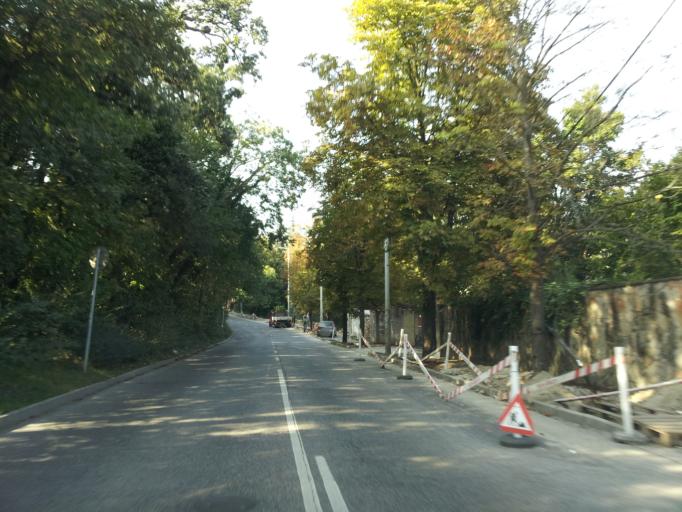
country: HU
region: Pest
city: Budakeszi
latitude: 47.5390
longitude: 18.9667
